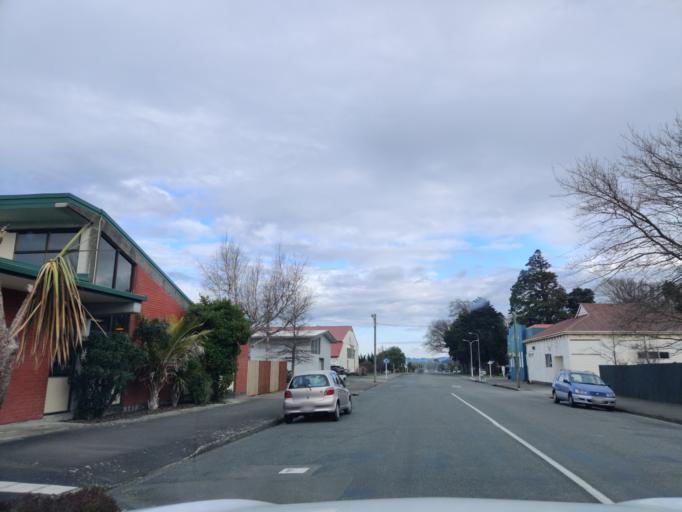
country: NZ
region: Manawatu-Wanganui
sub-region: Palmerston North City
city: Palmerston North
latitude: -40.3380
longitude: 175.8694
